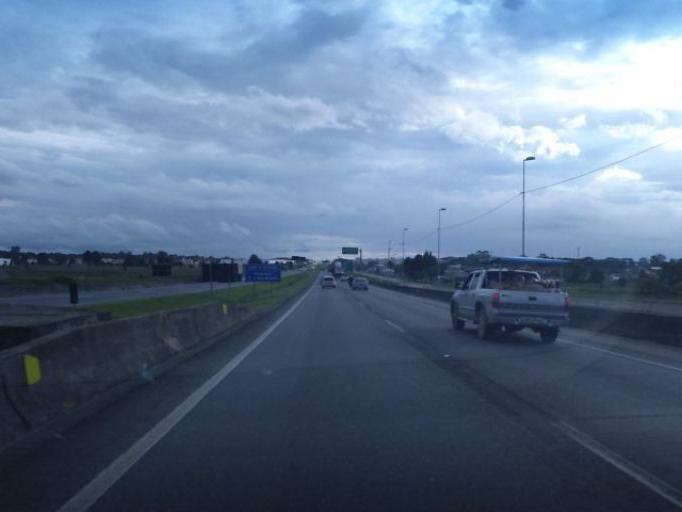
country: BR
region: Parana
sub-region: Piraquara
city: Piraquara
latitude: -25.5016
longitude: -49.1208
